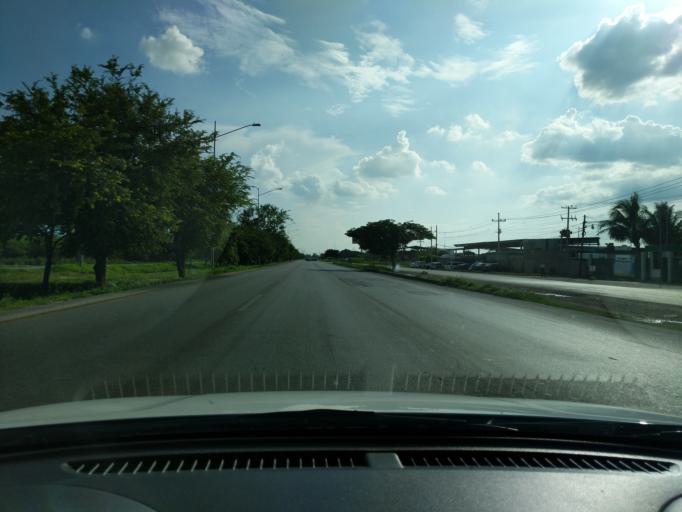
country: MX
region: Yucatan
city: Itzincab Palomeque
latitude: 20.9620
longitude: -89.6944
